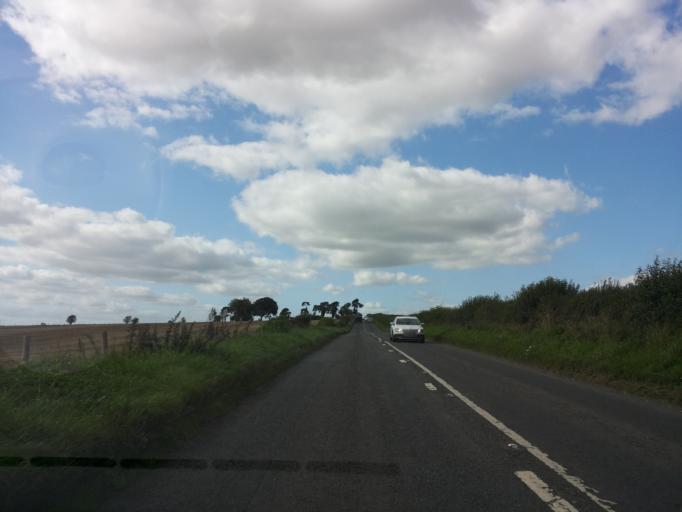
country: GB
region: England
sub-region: Wiltshire
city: Shrewton
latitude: 51.1866
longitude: -1.8804
